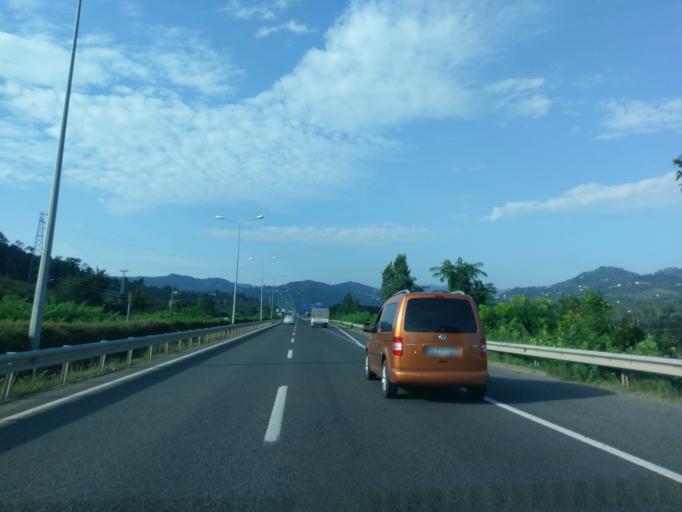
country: TR
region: Ordu
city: Ordu
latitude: 41.0100
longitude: 37.8309
